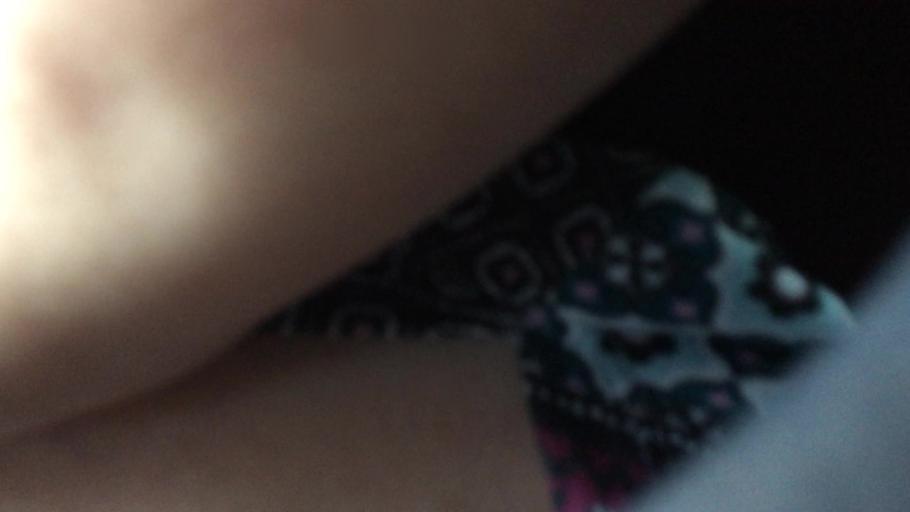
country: US
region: New Mexico
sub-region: Colfax County
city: Springer
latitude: 36.3389
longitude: -104.6126
